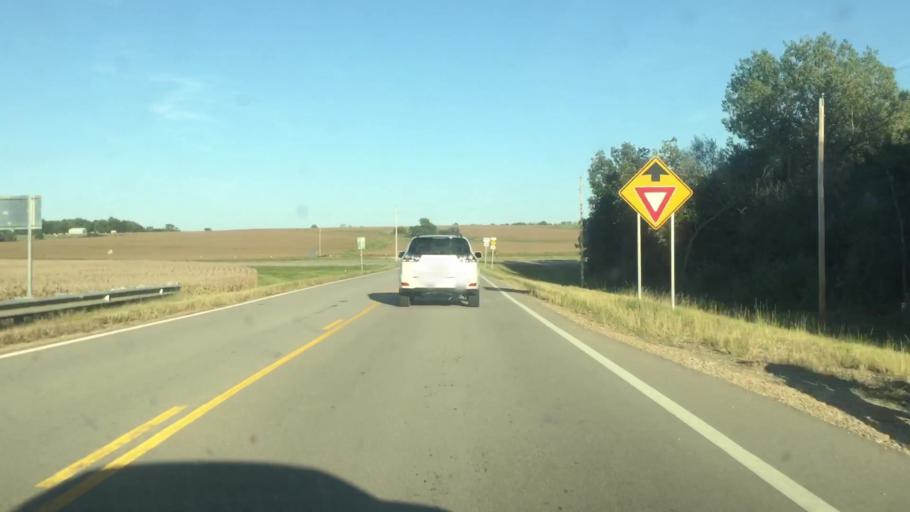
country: US
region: Kansas
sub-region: Brown County
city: Horton
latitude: 39.5874
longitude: -95.5297
